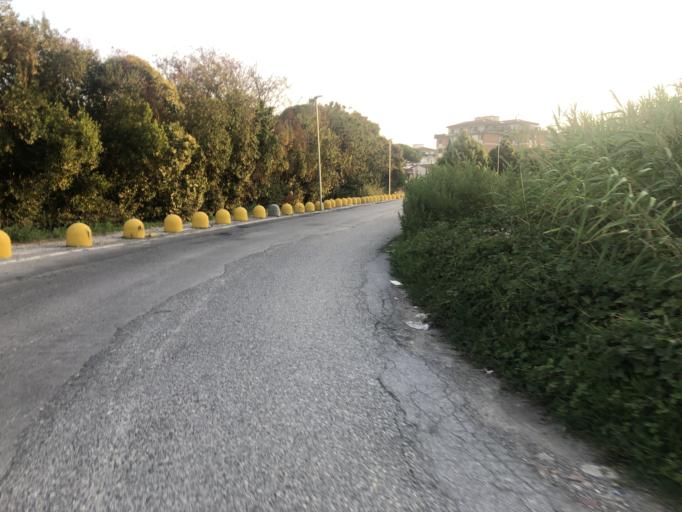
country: IT
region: Tuscany
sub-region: Province of Pisa
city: Pisa
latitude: 43.7230
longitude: 10.4173
